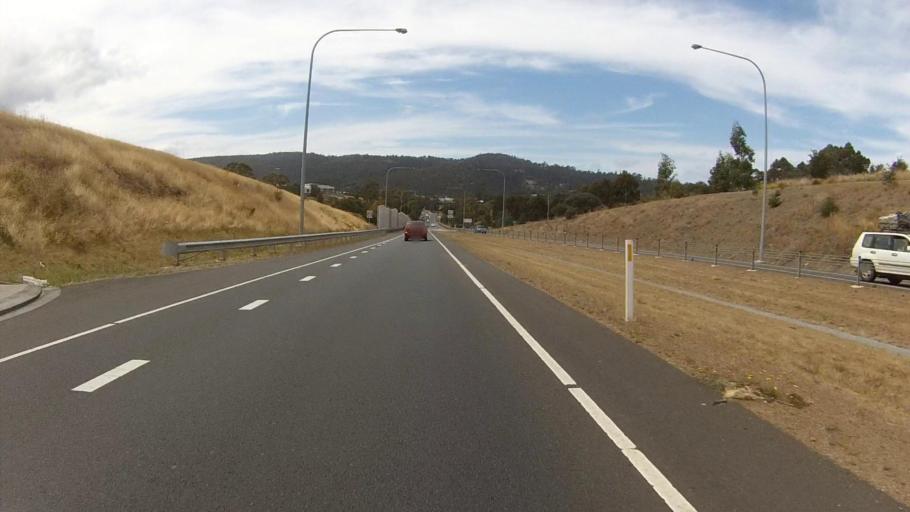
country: AU
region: Tasmania
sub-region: Kingborough
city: Kingston
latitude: -42.9746
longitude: 147.3032
